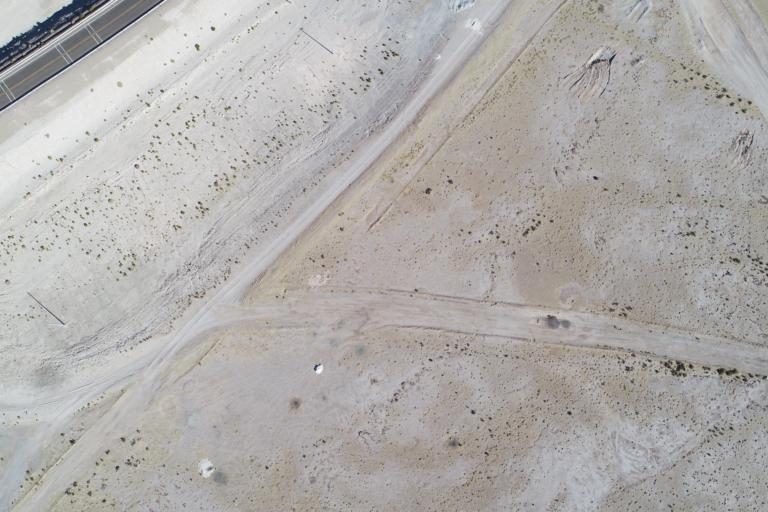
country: BO
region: Potosi
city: Colchani
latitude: -20.3534
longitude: -66.9040
